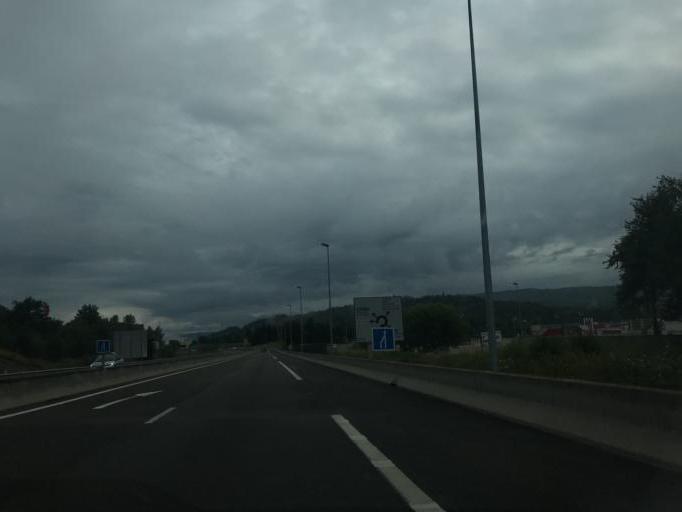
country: FR
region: Rhone-Alpes
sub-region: Departement de l'Ain
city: Arbent
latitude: 46.2813
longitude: 5.6603
